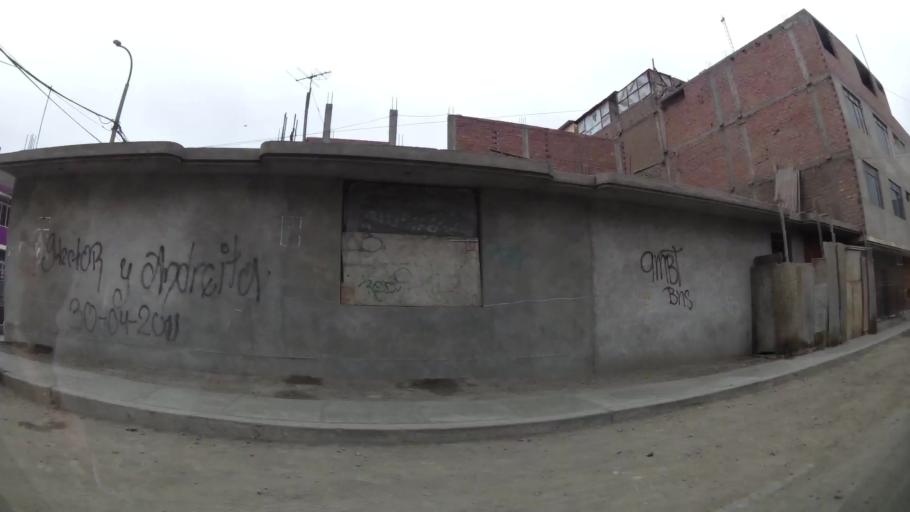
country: PE
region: Lima
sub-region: Lima
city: Independencia
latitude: -11.9658
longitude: -77.0609
